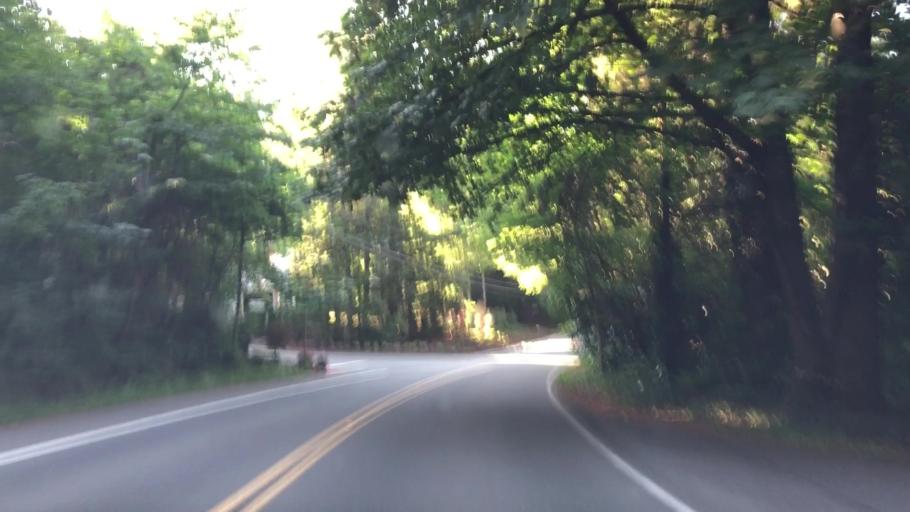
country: US
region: Washington
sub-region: King County
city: Woodinville
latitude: 47.7593
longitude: -122.1260
